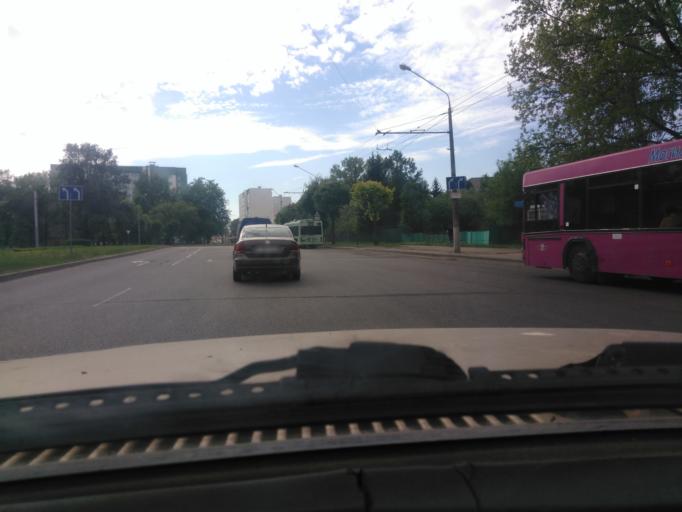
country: BY
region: Mogilev
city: Buynichy
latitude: 53.8979
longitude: 30.2939
